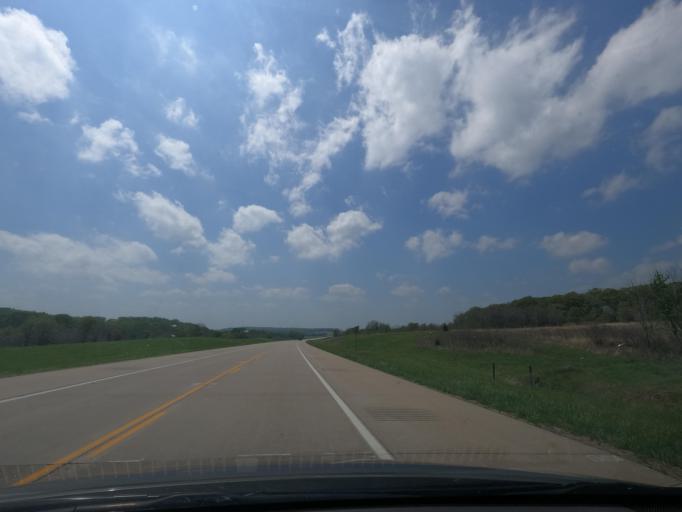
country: US
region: Kansas
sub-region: Wilson County
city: Fredonia
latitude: 37.6136
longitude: -95.9317
